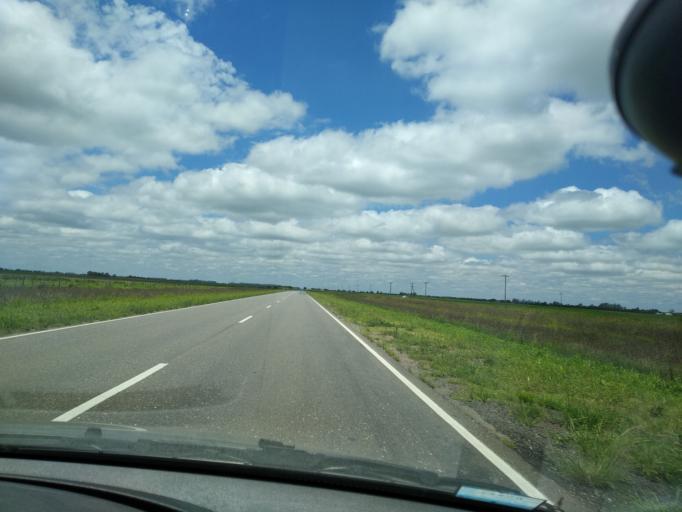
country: AR
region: Cordoba
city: Toledo
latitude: -31.6453
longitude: -64.0176
